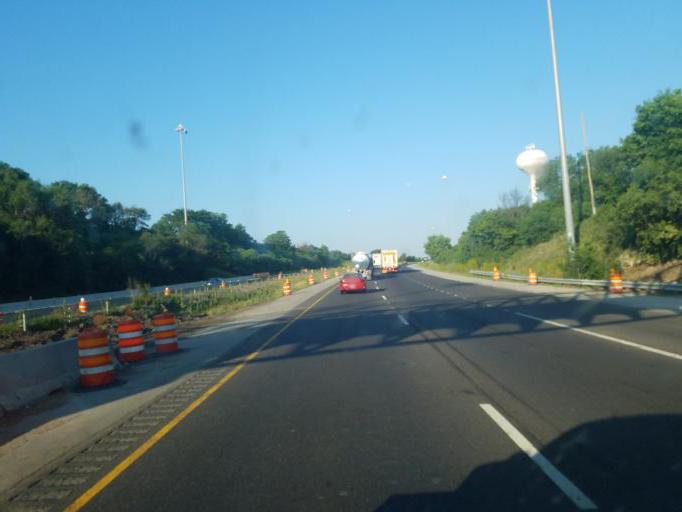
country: US
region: Illinois
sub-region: Will County
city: New Lenox
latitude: 41.5169
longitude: -87.9951
